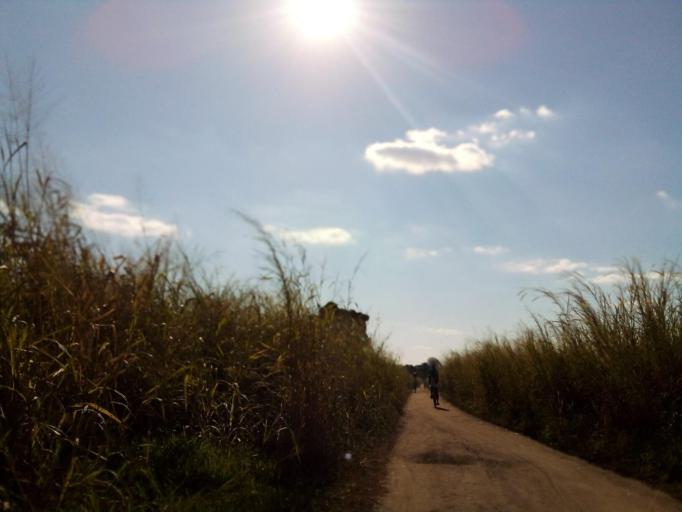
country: MZ
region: Zambezia
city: Quelimane
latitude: -17.5440
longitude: 36.6934
